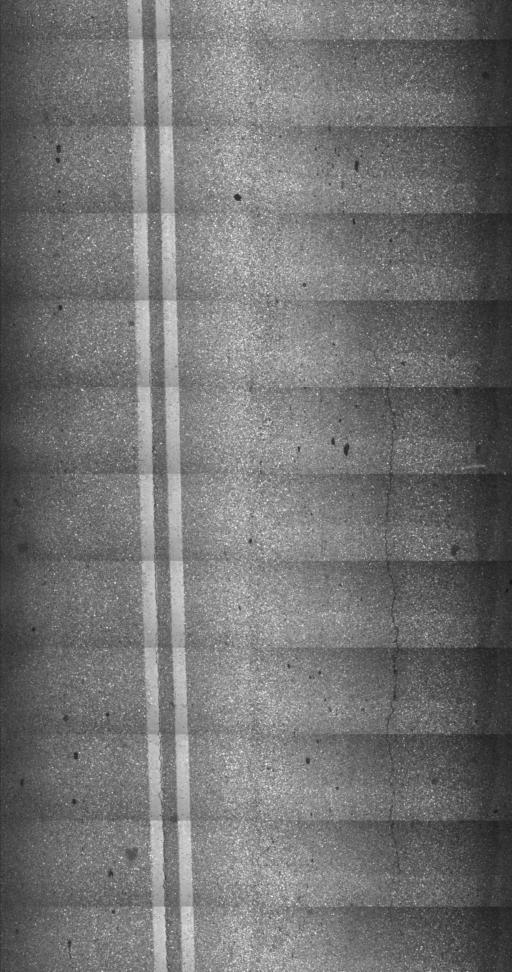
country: US
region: New York
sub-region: Essex County
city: Port Henry
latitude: 44.0269
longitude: -73.3990
